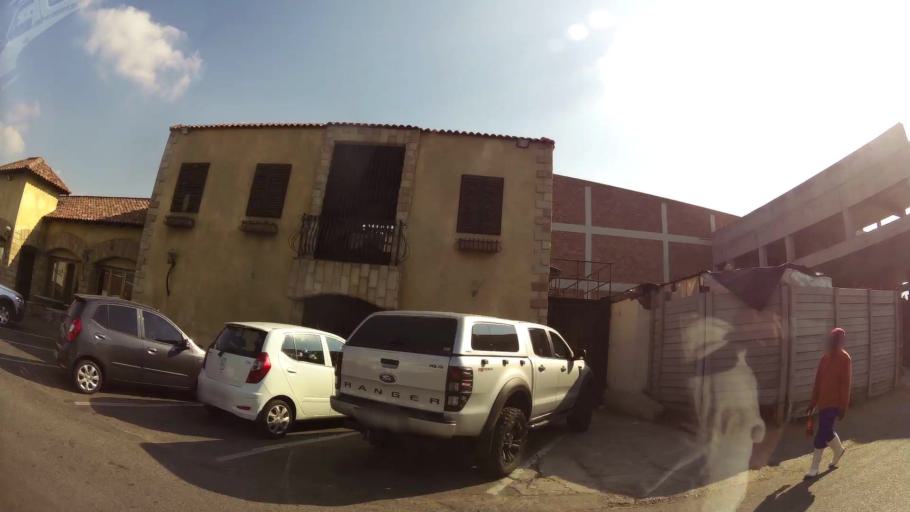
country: ZA
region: Gauteng
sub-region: Ekurhuleni Metropolitan Municipality
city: Boksburg
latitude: -26.2032
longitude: 28.2594
